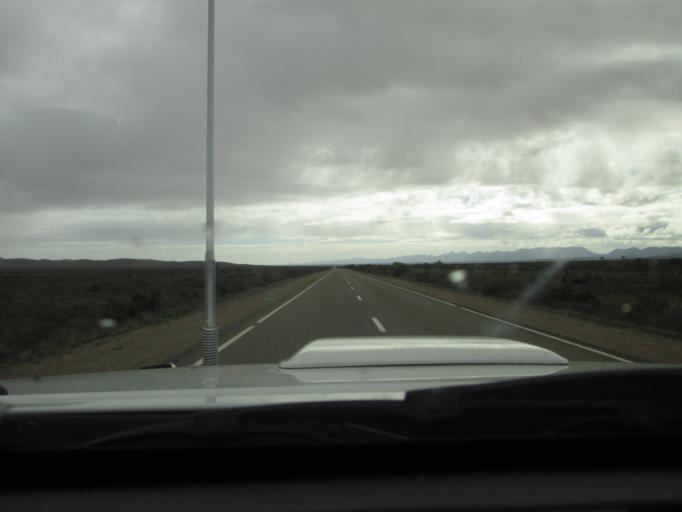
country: AU
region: South Australia
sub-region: Flinders Ranges
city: Quorn
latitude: -31.5273
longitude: 138.4264
